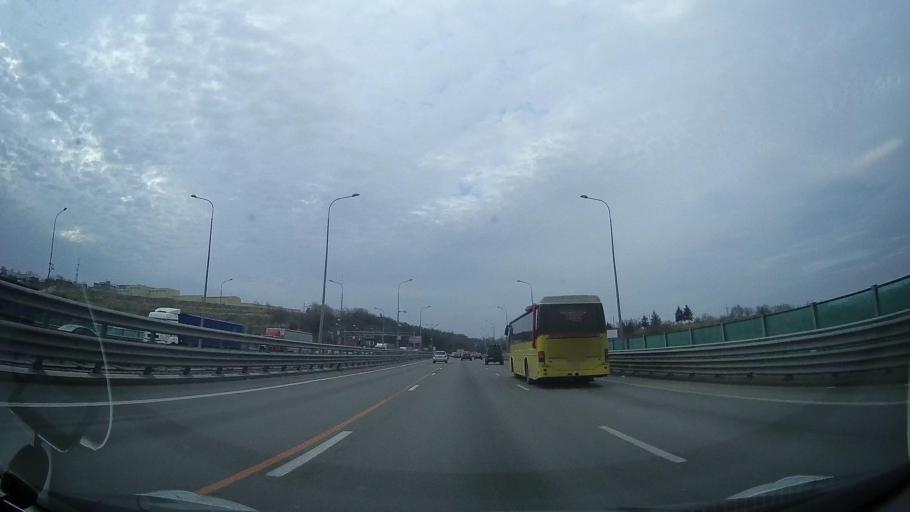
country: RU
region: Rostov
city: Aksay
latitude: 47.2429
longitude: 39.8502
